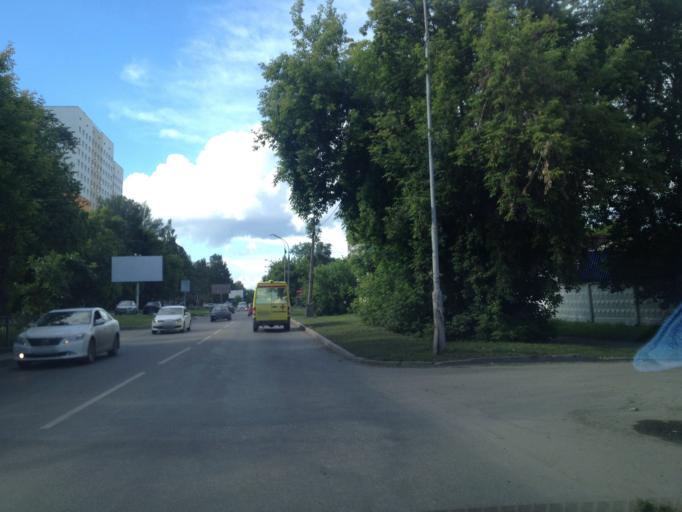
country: RU
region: Sverdlovsk
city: Yekaterinburg
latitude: 56.8359
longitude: 60.6616
